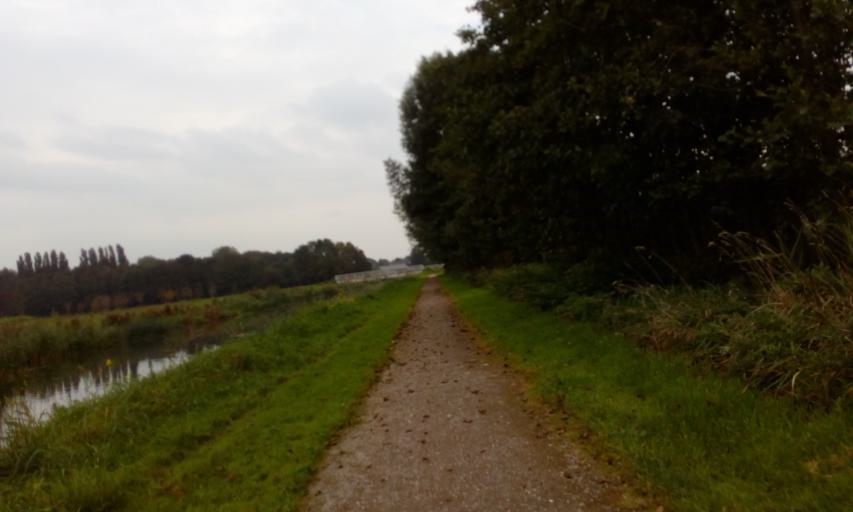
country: NL
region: South Holland
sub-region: Gemeente Lansingerland
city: Bleiswijk
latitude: 51.9893
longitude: 4.5404
